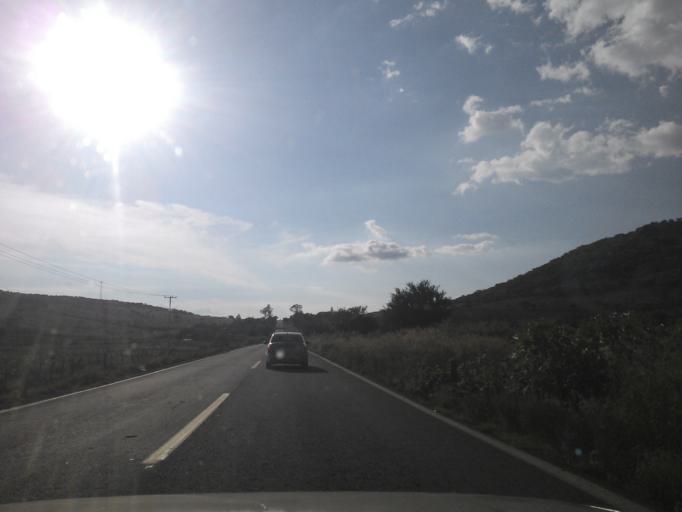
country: MX
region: Jalisco
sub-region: Tototlan
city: Nuevo Refugio de Afuera (Nuevo Refugio)
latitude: 20.5459
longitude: -102.6418
